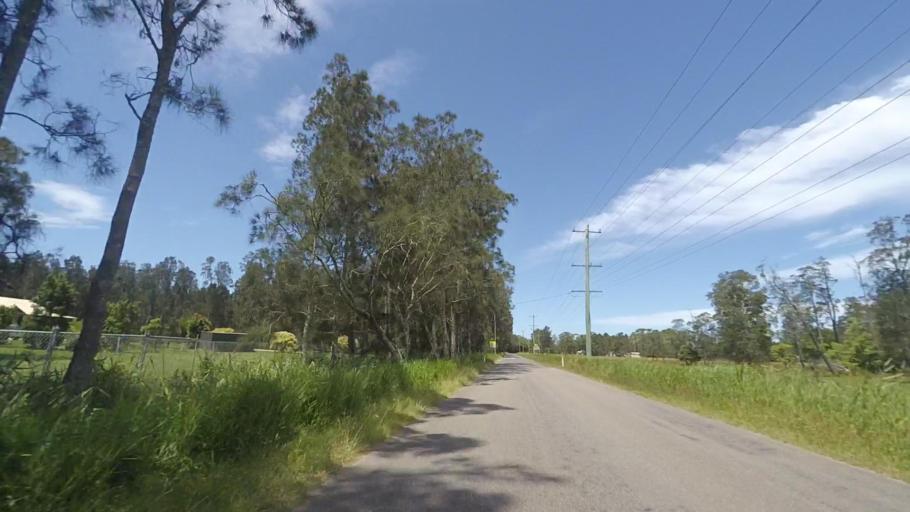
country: AU
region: New South Wales
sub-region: Port Stephens Shire
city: Port Stephens
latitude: -32.7667
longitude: 152.0067
